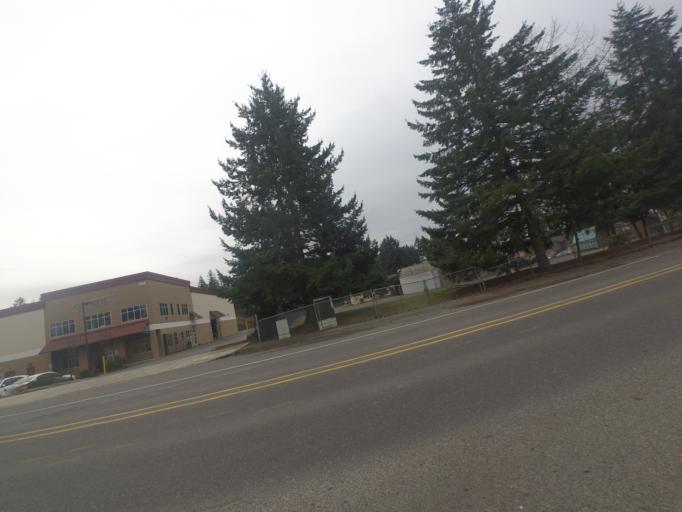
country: US
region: Washington
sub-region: Pierce County
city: McChord Air Force Base
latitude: 47.1213
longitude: -122.5314
